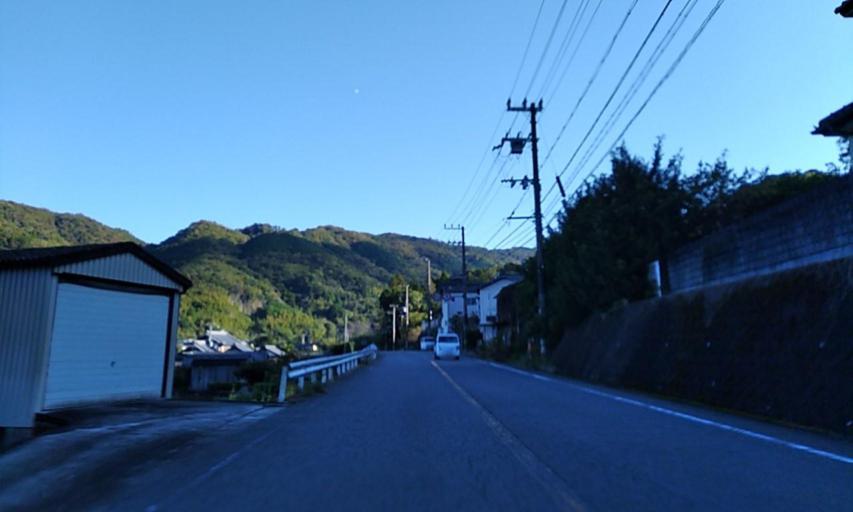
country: JP
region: Wakayama
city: Iwade
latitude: 34.1530
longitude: 135.3186
